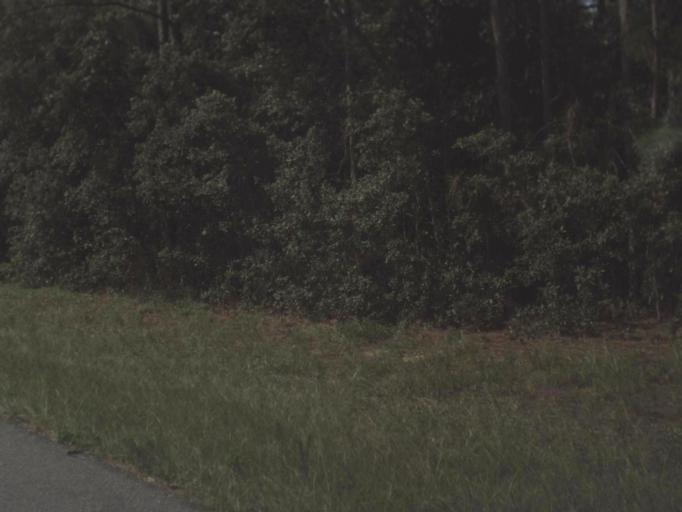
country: US
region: Florida
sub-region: Citrus County
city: Citrus Springs
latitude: 28.9853
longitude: -82.4341
